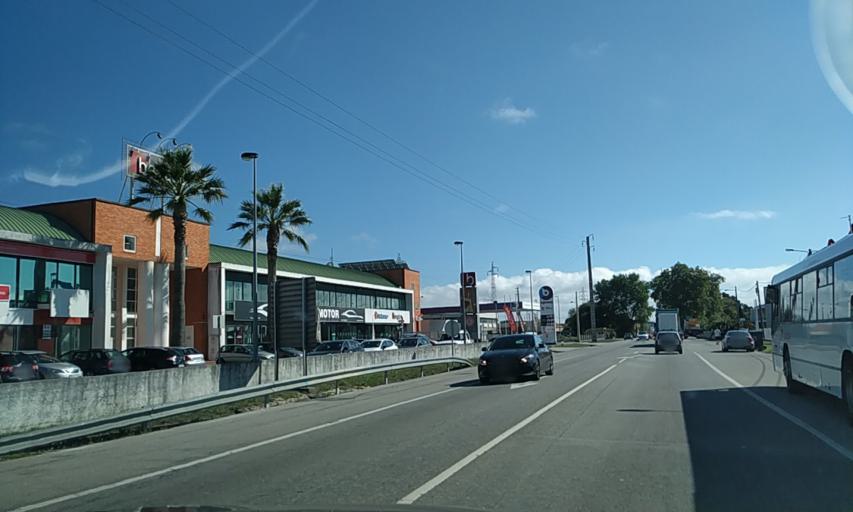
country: PT
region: Aveiro
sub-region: Aveiro
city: Aveiro
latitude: 40.6624
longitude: -8.6124
